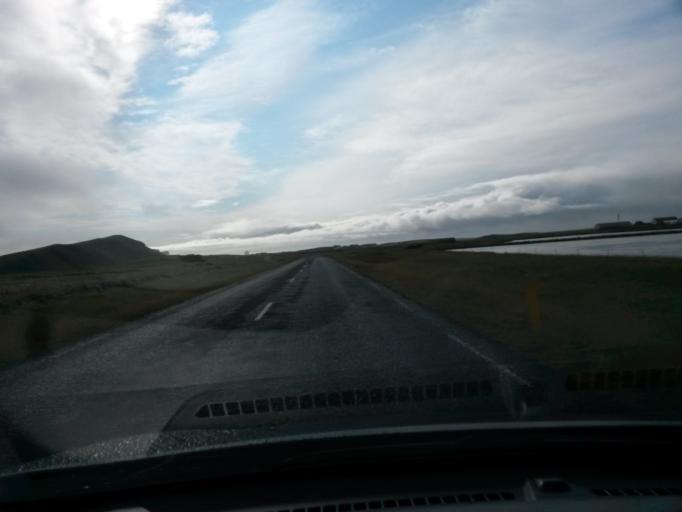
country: IS
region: South
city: Vestmannaeyjar
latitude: 63.4371
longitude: -19.1941
